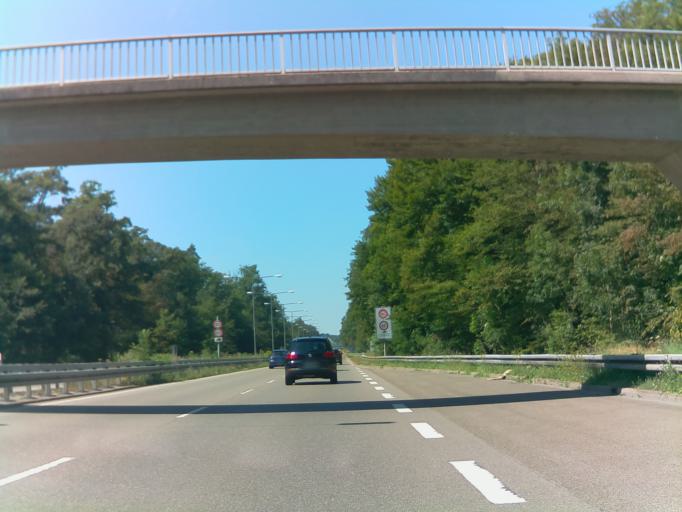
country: DE
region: Baden-Wuerttemberg
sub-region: Regierungsbezirk Stuttgart
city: Gerlingen
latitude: 48.7691
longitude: 9.1083
